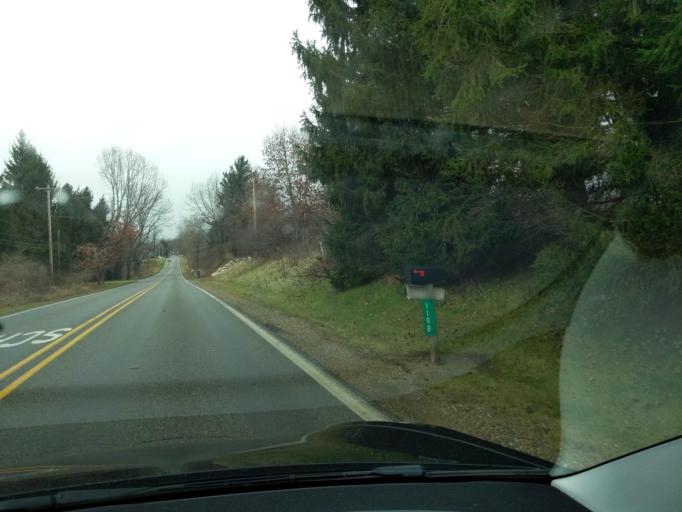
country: US
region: Michigan
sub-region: Jackson County
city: Spring Arbor
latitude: 42.2478
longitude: -84.5374
